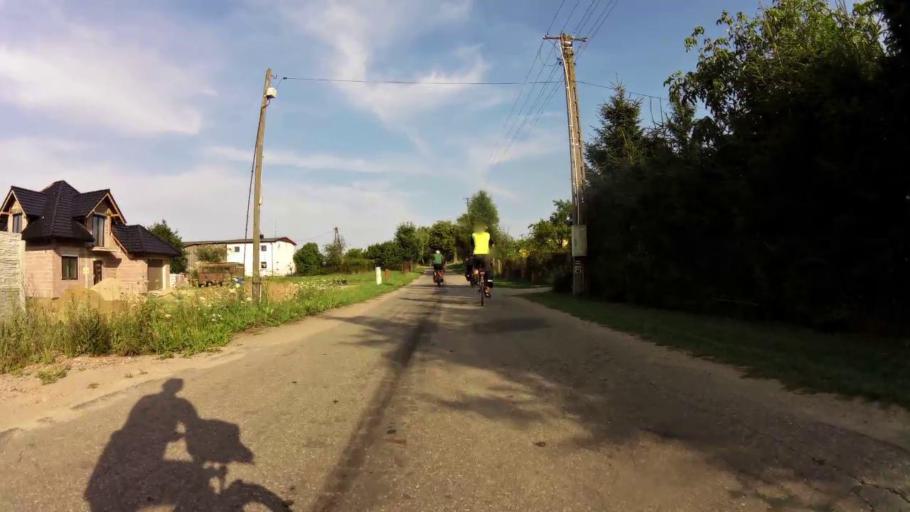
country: PL
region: West Pomeranian Voivodeship
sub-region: Powiat drawski
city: Drawsko Pomorskie
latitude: 53.4924
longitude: 15.7848
